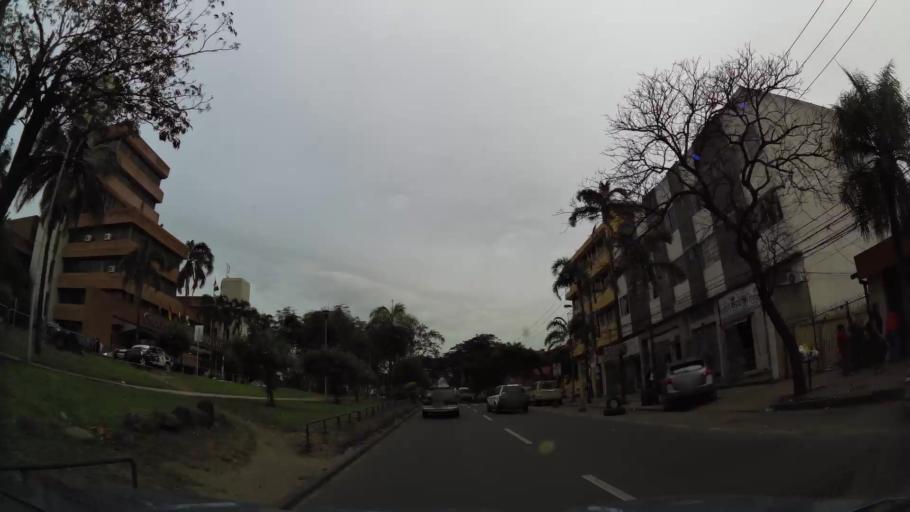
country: BO
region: Santa Cruz
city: Santa Cruz de la Sierra
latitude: -17.7965
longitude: -63.1865
